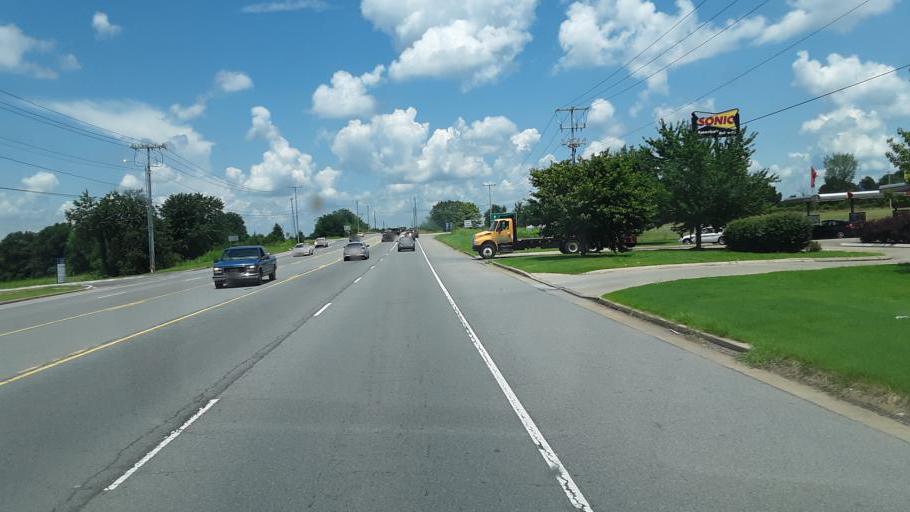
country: US
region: Tennessee
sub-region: Montgomery County
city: Clarksville
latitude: 36.6262
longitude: -87.3175
